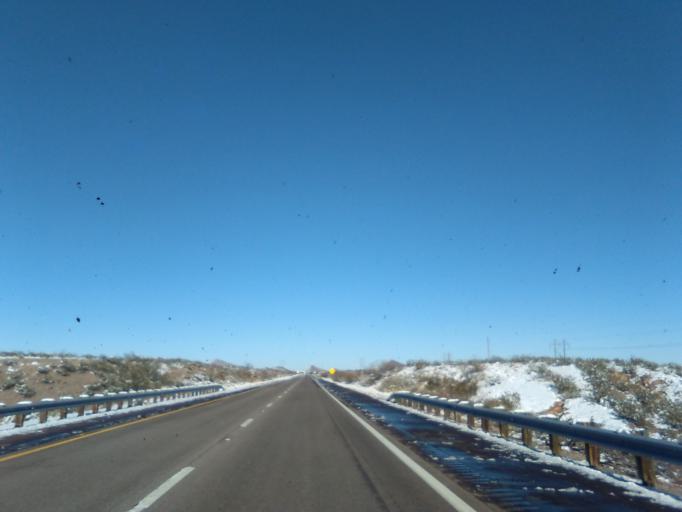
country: US
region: New Mexico
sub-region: Socorro County
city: Socorro
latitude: 33.7100
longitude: -107.0398
